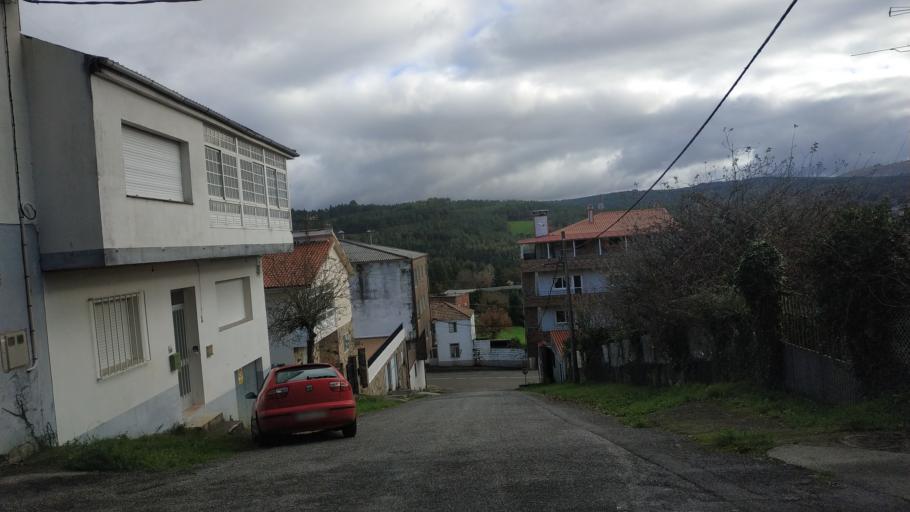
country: ES
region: Galicia
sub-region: Provincia de Pontevedra
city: Silleda
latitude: 42.7926
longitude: -8.1723
